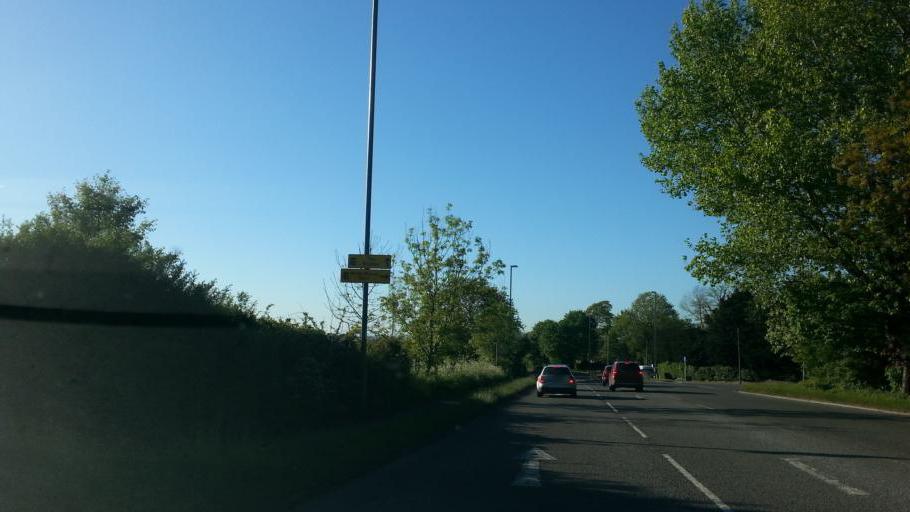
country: GB
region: England
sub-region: Bath and North East Somerset
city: Whitchurch
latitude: 51.4009
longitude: -2.5523
